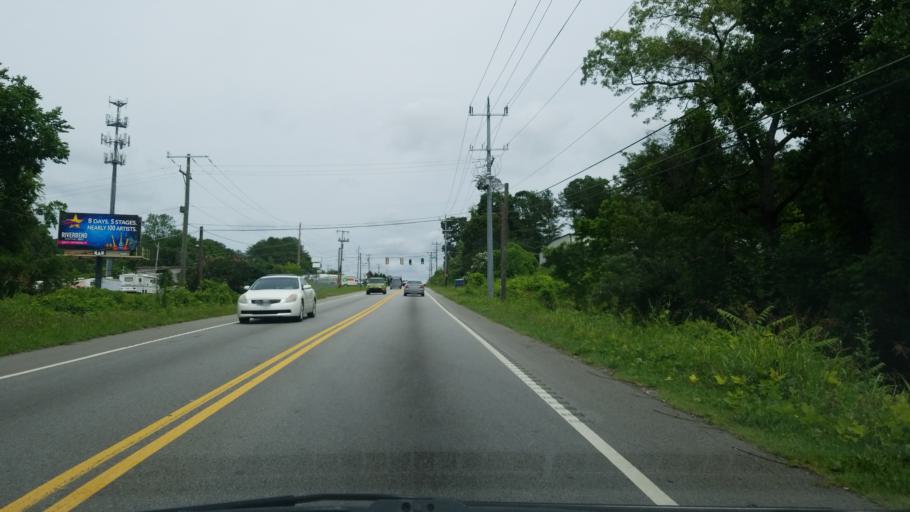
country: US
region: Tennessee
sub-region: Hamilton County
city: Harrison
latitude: 35.0744
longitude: -85.1724
